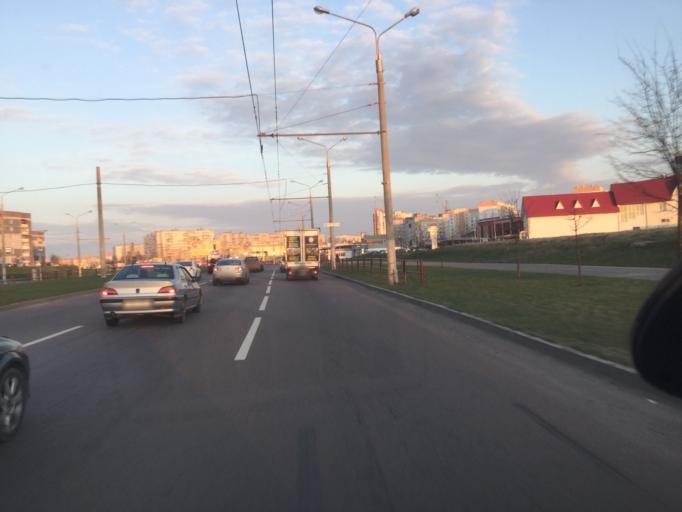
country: BY
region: Vitebsk
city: Vitebsk
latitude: 55.1653
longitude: 30.2012
